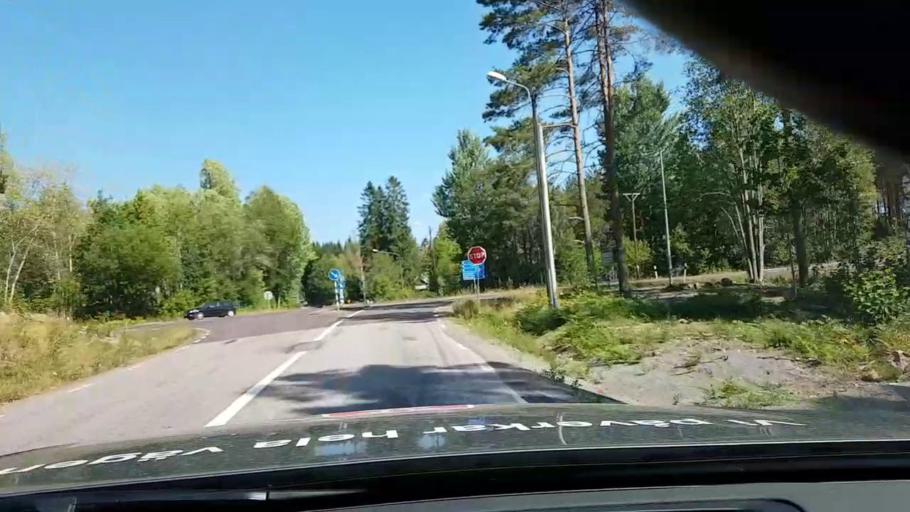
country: SE
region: Kalmar
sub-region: Hultsfreds Kommun
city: Virserum
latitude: 57.1386
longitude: 15.6597
